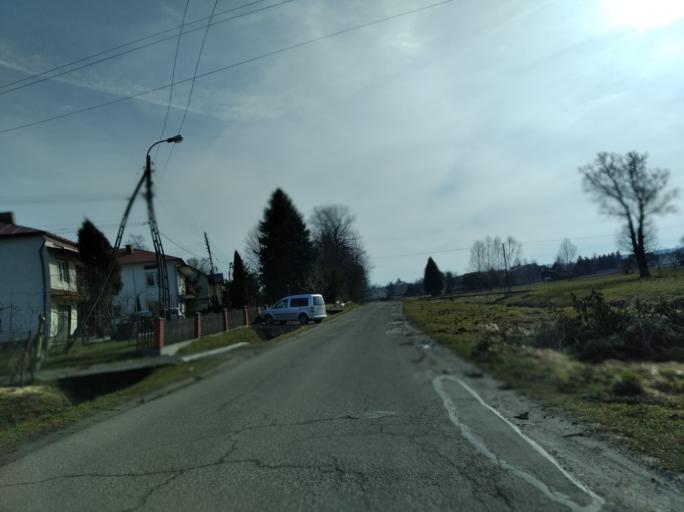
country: PL
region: Subcarpathian Voivodeship
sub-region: Powiat brzozowski
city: Humniska
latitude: 49.6723
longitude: 22.0523
